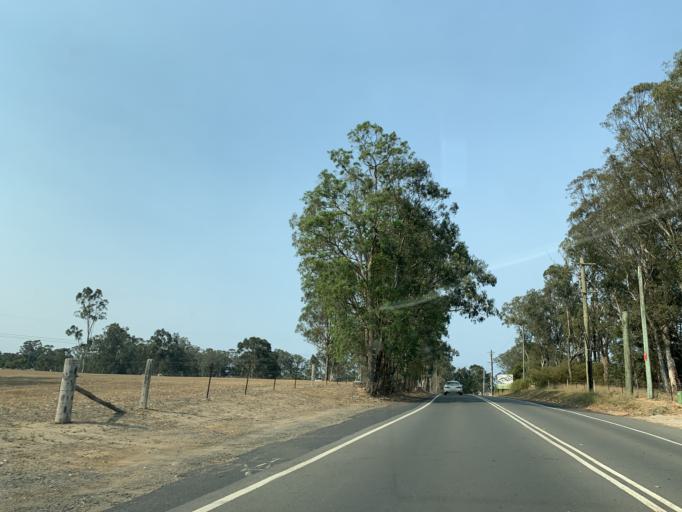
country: AU
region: New South Wales
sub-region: Blacktown
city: Rouse Hill
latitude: -33.6649
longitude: 150.9192
